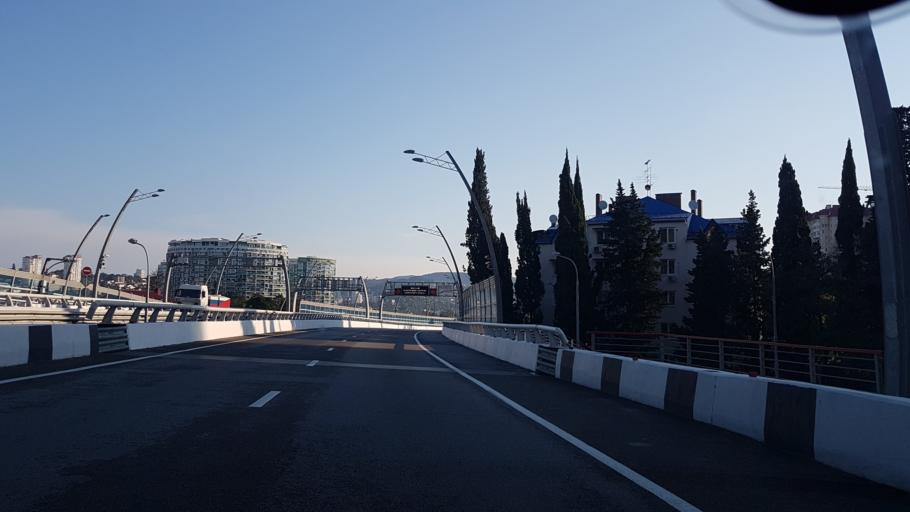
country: RU
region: Krasnodarskiy
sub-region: Sochi City
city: Sochi
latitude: 43.5902
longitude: 39.7305
